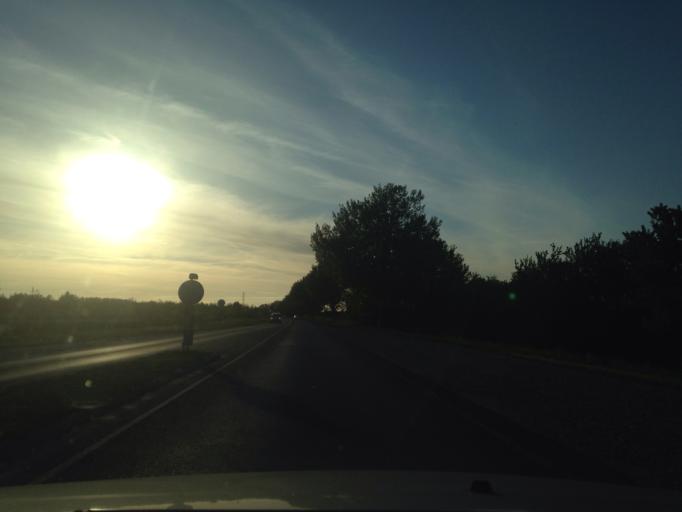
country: DK
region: Zealand
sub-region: Greve Kommune
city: Tune
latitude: 55.5998
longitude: 12.2255
